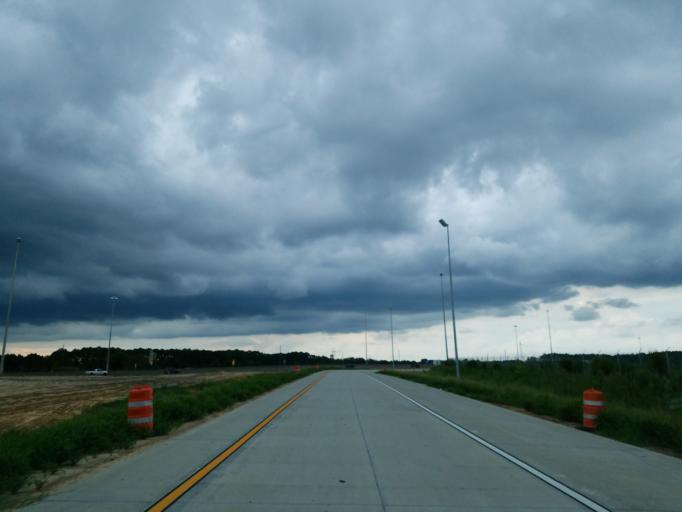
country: US
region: Georgia
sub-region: Tift County
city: Tifton
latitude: 31.5024
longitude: -83.5172
